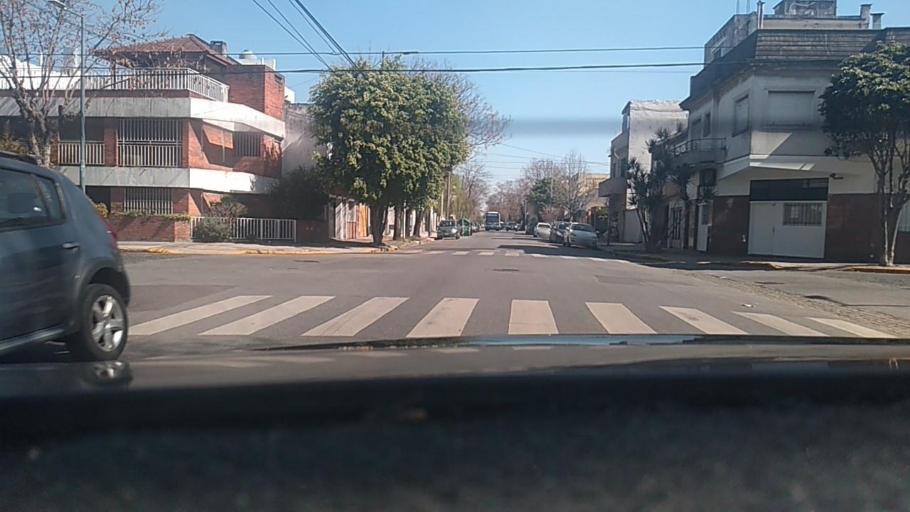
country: AR
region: Buenos Aires F.D.
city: Villa Santa Rita
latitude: -34.6080
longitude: -58.4959
